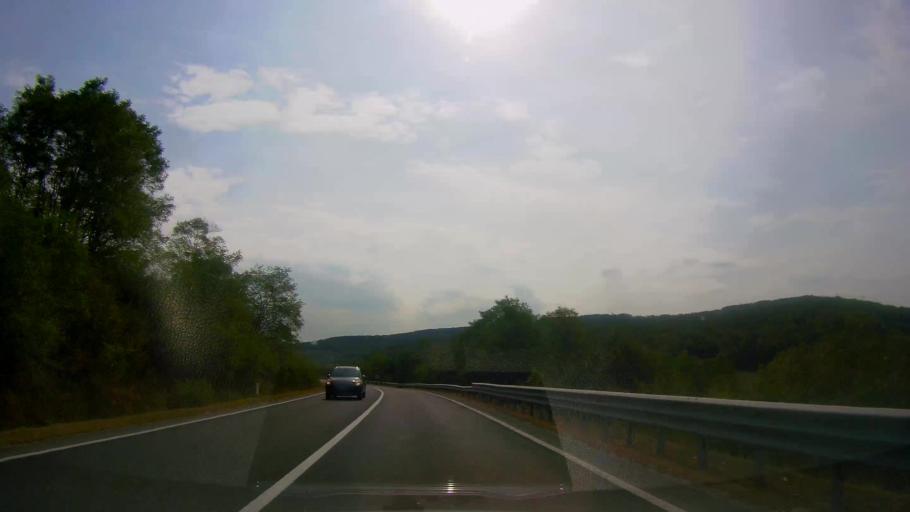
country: RO
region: Salaj
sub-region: Comuna Zimbor
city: Zimbor
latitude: 46.9745
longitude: 23.2558
